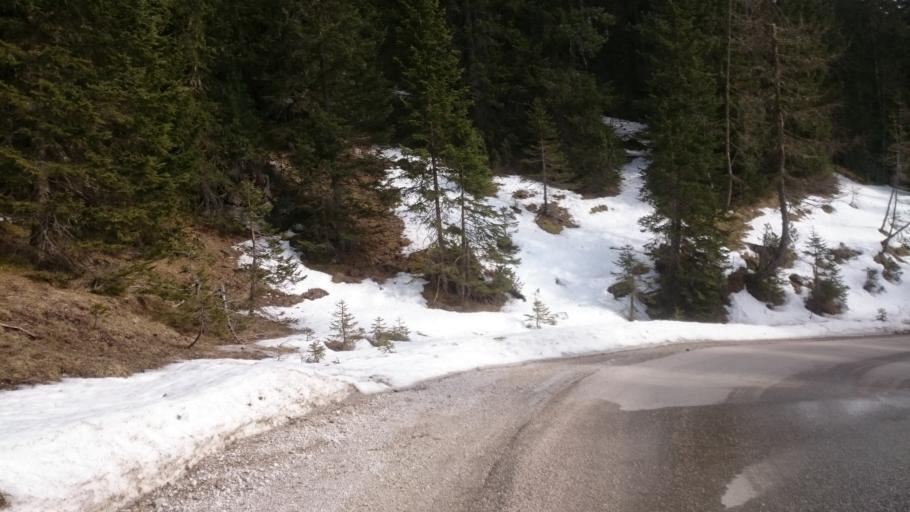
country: IT
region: Trentino-Alto Adige
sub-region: Bolzano
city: Braies
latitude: 46.6615
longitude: 12.1678
